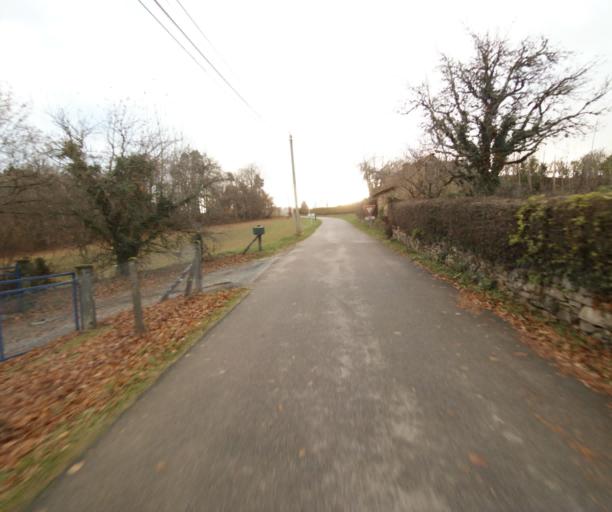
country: FR
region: Limousin
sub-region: Departement de la Correze
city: Sainte-Fortunade
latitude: 45.2134
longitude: 1.7808
